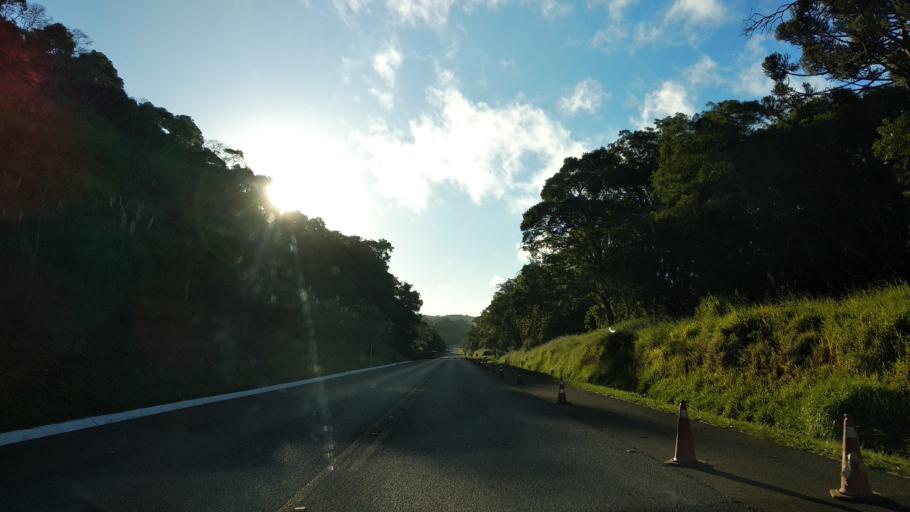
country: BR
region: Santa Catarina
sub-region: Correia Pinto
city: Correia Pinto
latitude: -27.6144
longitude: -50.7149
